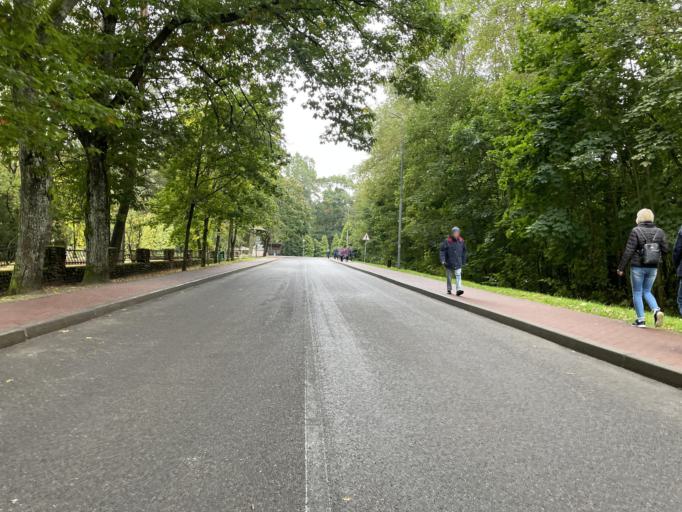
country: BY
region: Brest
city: Kamyanyuki
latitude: 52.5707
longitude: 23.8022
